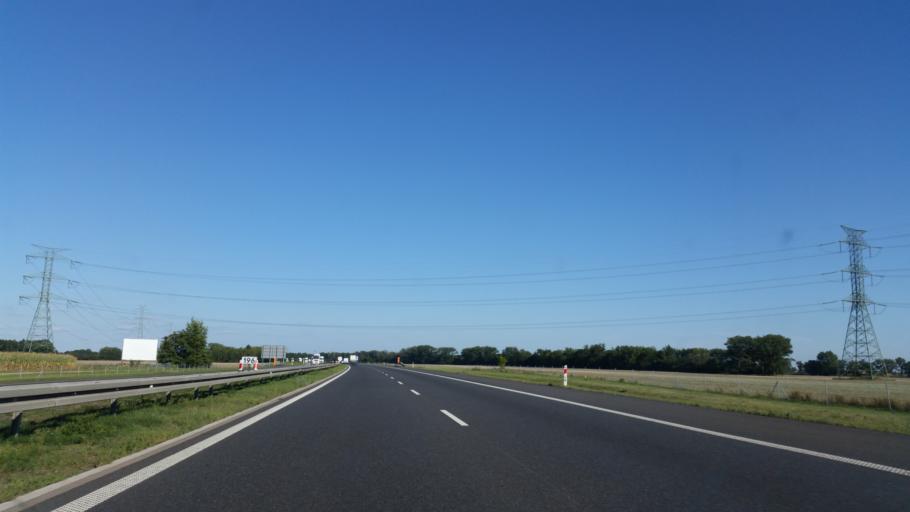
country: PL
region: Opole Voivodeship
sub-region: Powiat brzeski
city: Grodkow
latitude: 50.7726
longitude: 17.3716
